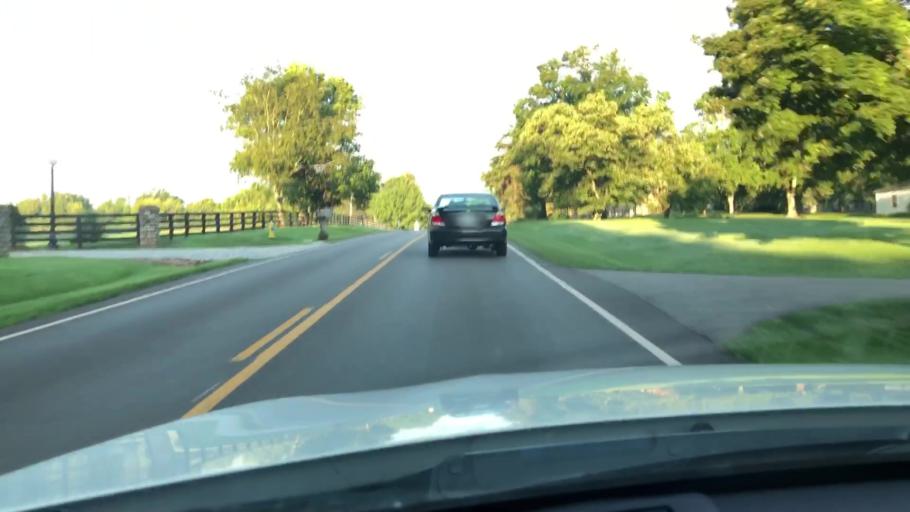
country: US
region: Kentucky
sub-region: Jefferson County
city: Middletown
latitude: 38.2189
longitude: -85.5209
